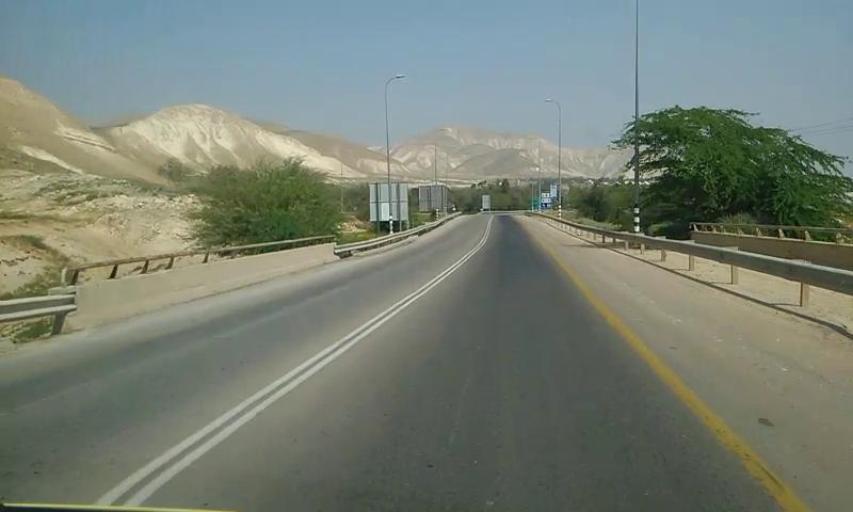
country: PS
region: West Bank
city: Al Fasayil
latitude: 32.0507
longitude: 35.4648
